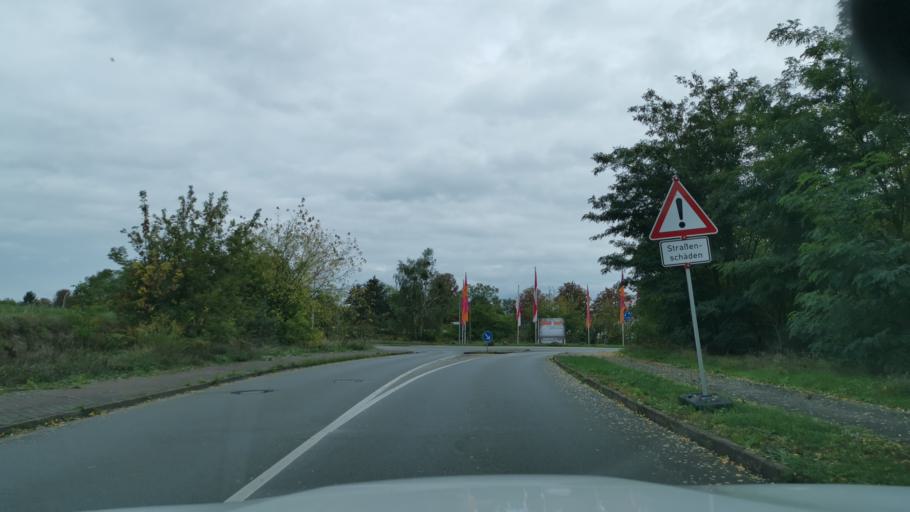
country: DE
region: Brandenburg
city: Wustermark
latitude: 52.4752
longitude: 12.9611
